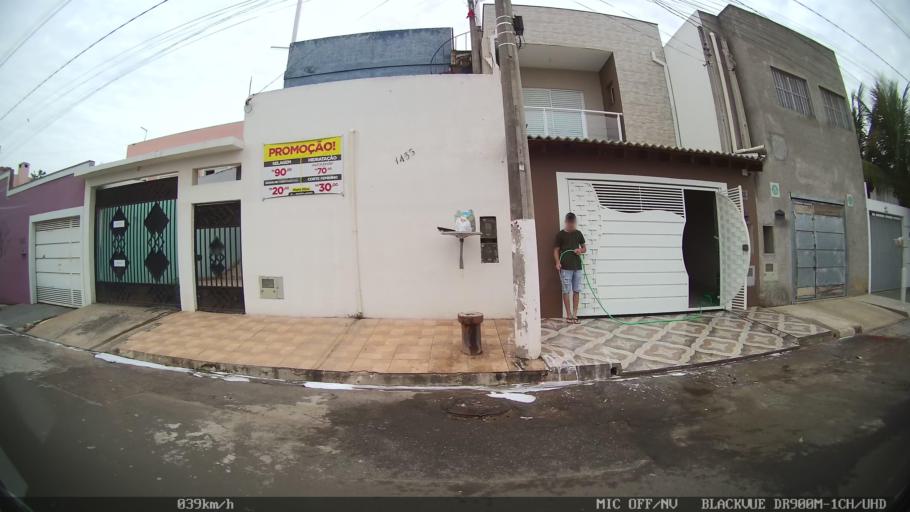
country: BR
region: Sao Paulo
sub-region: Paulinia
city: Paulinia
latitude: -22.7195
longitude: -47.1672
